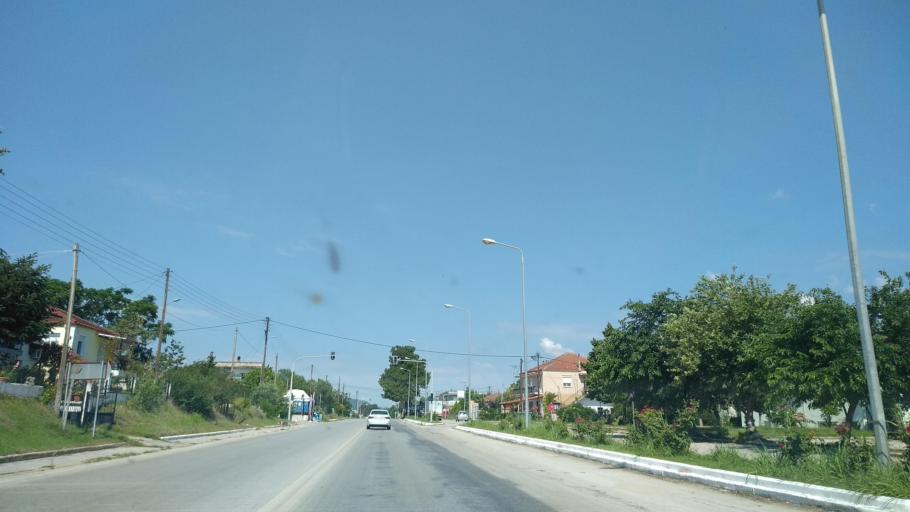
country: GR
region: Central Macedonia
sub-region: Nomos Thessalonikis
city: Nea Apollonia
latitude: 40.6386
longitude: 23.4877
